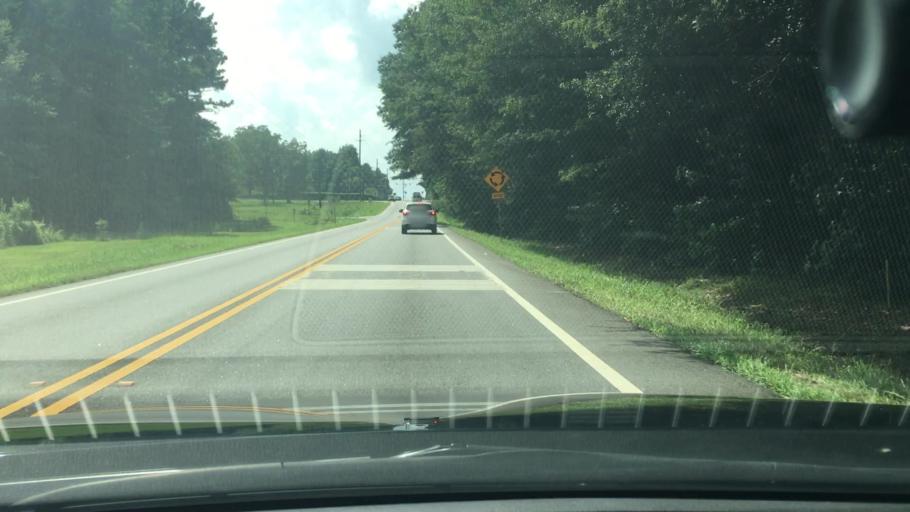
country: US
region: Georgia
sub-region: Fayette County
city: Peachtree City
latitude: 33.3289
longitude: -84.6422
